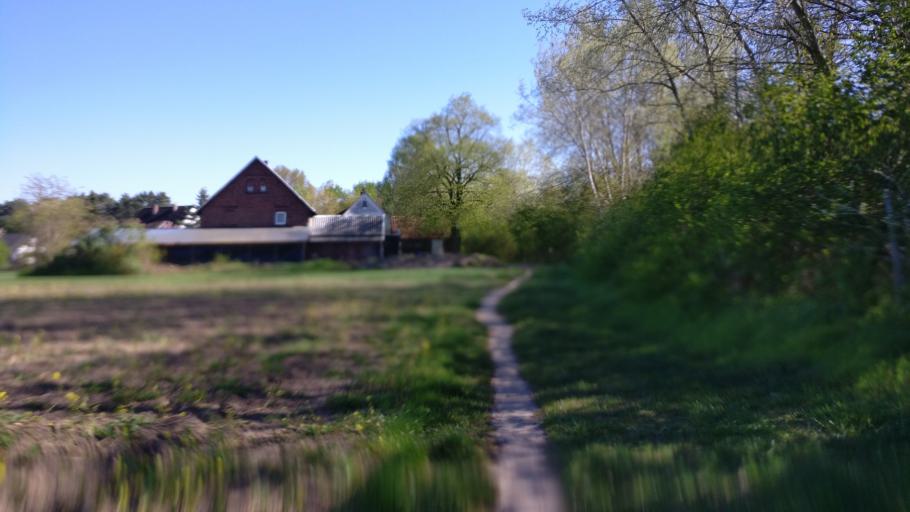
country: DE
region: North Rhine-Westphalia
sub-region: Regierungsbezirk Detmold
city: Lage
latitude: 52.0167
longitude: 8.7605
